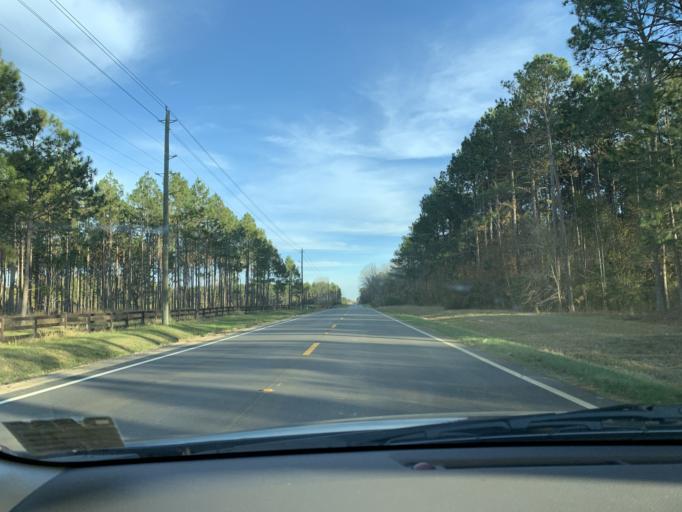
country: US
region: Georgia
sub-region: Irwin County
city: Ocilla
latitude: 31.5839
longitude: -83.0727
